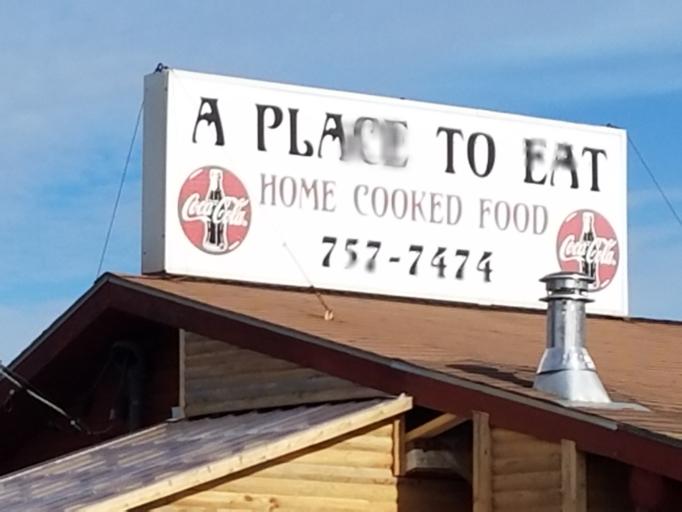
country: US
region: Maine
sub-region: Aroostook County
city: Hodgdon
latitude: 46.1117
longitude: -68.1603
